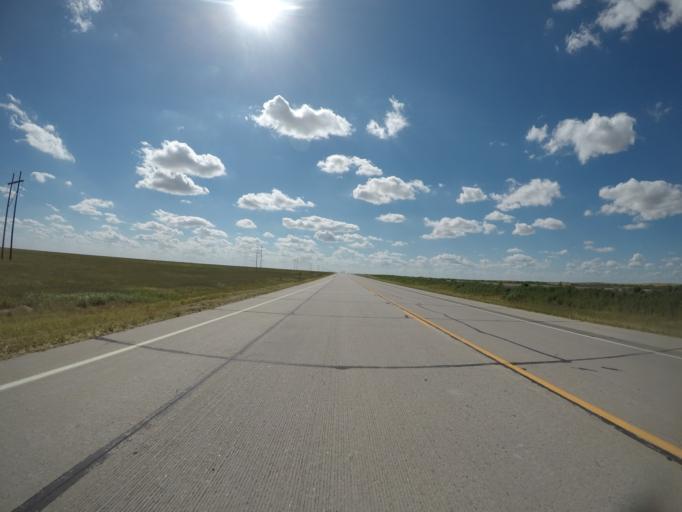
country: US
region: Colorado
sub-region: Phillips County
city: Holyoke
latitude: 40.6004
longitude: -102.4001
